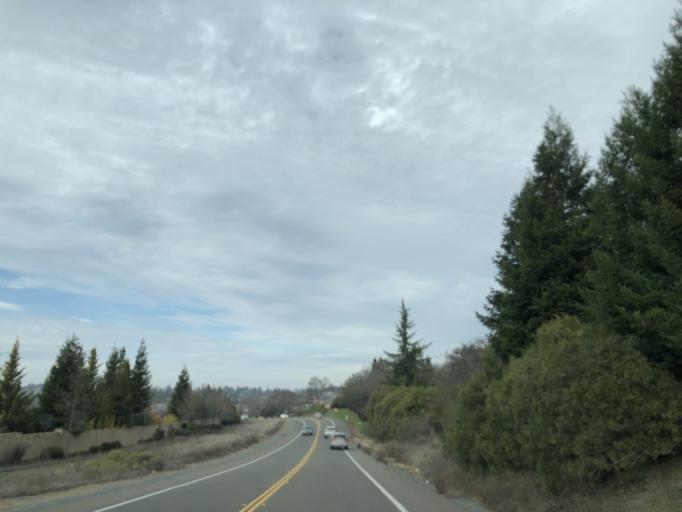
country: US
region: California
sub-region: El Dorado County
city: El Dorado Hills
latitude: 38.7058
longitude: -121.0840
